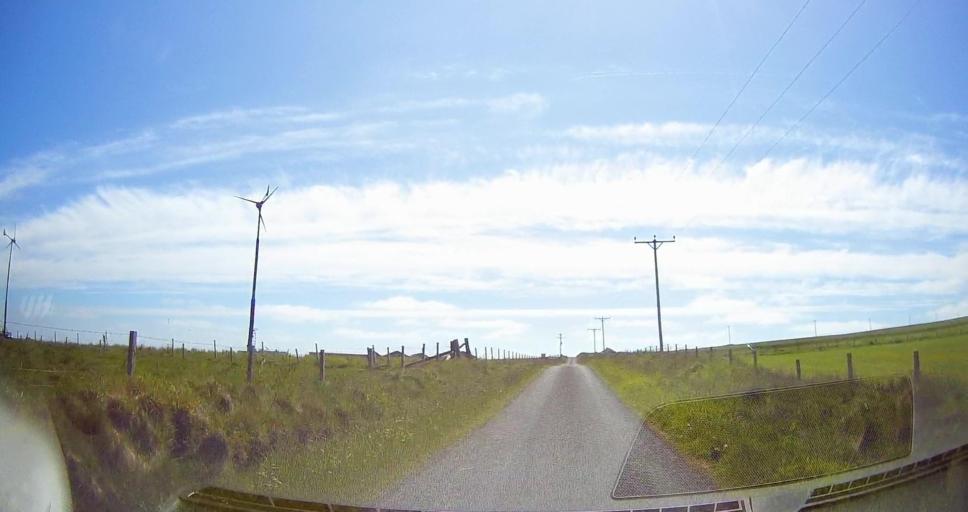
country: GB
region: Scotland
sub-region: Orkney Islands
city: Kirkwall
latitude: 58.8227
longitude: -2.9079
